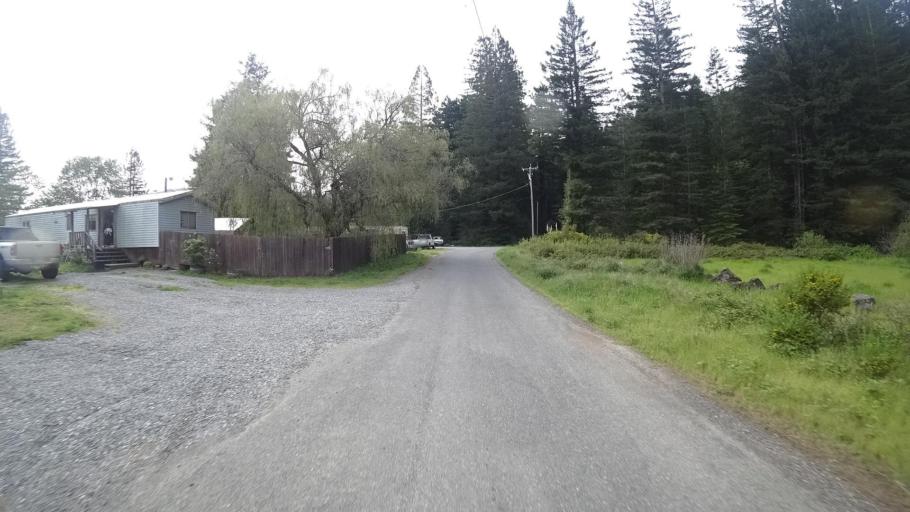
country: US
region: California
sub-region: Humboldt County
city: Redway
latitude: 40.3443
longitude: -123.9166
